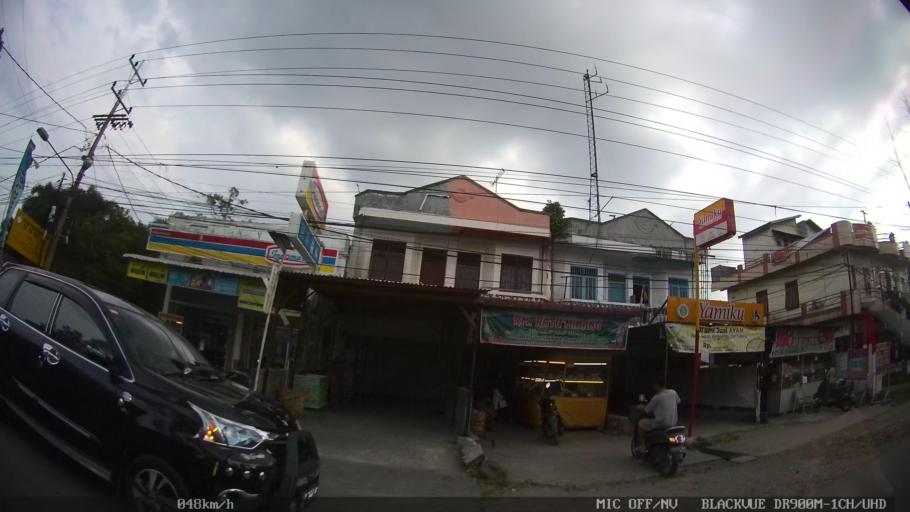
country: ID
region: North Sumatra
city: Sunggal
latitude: 3.5401
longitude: 98.6263
